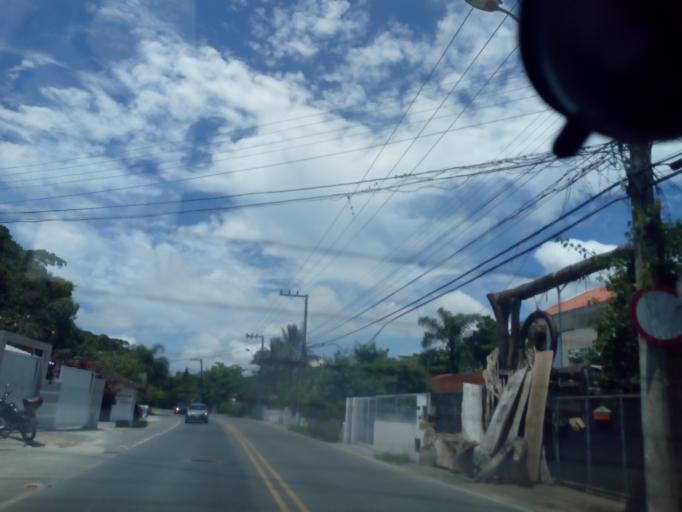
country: BR
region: Santa Catarina
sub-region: Florianopolis
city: Itacorubi
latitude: -27.4044
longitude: -48.4267
